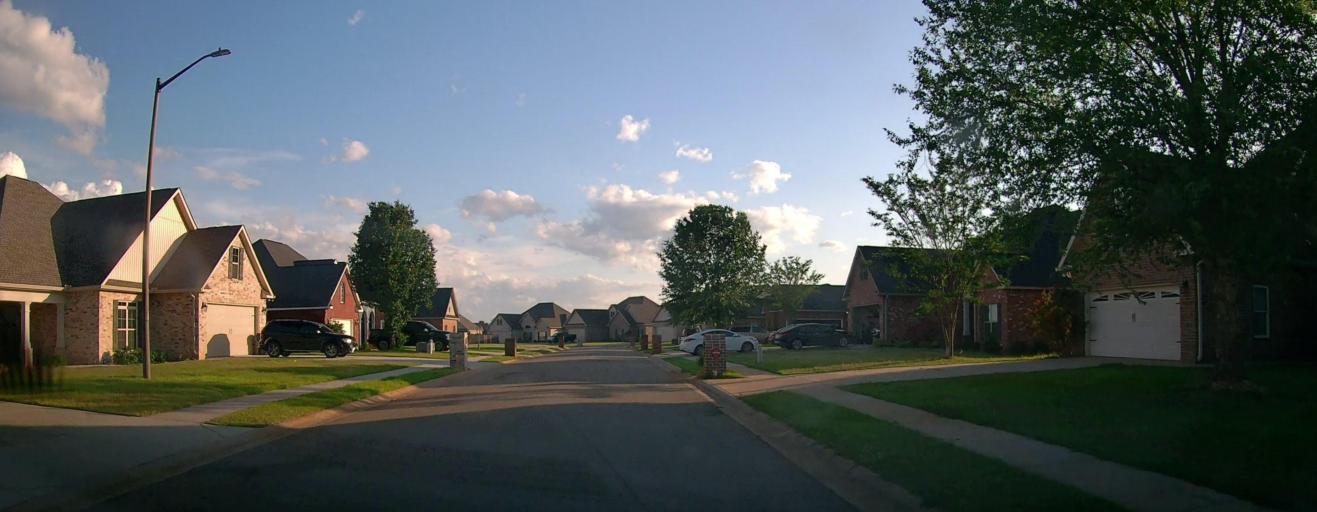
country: US
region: Georgia
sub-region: Houston County
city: Centerville
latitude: 32.6303
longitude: -83.7204
